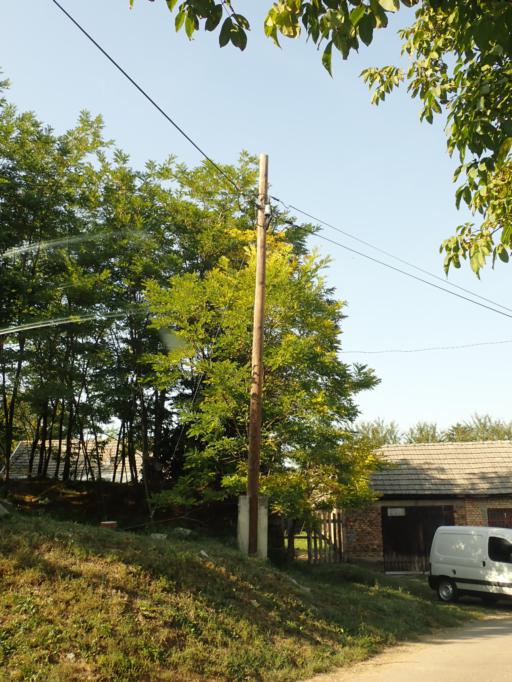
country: HU
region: Baranya
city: Boly
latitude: 45.9955
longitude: 18.5106
